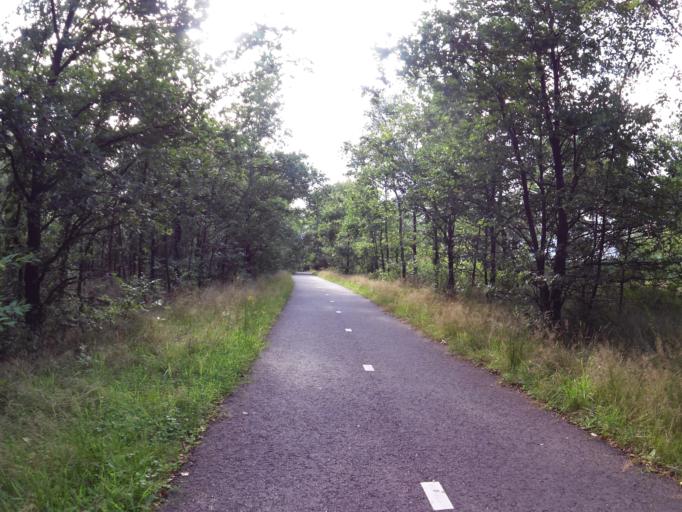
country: NL
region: Gelderland
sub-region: Gemeente Rozendaal
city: Rozendaal
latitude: 52.0380
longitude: 5.9215
